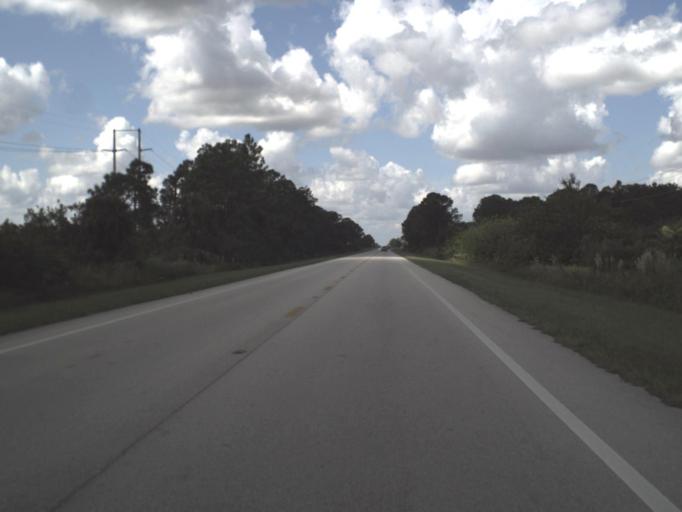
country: US
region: Florida
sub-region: Lee County
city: Lehigh Acres
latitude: 26.5114
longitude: -81.5358
